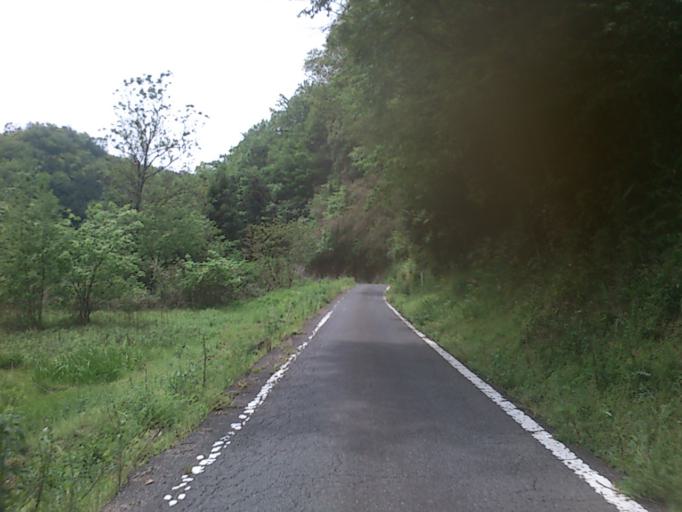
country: JP
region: Kyoto
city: Miyazu
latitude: 35.6071
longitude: 135.1100
